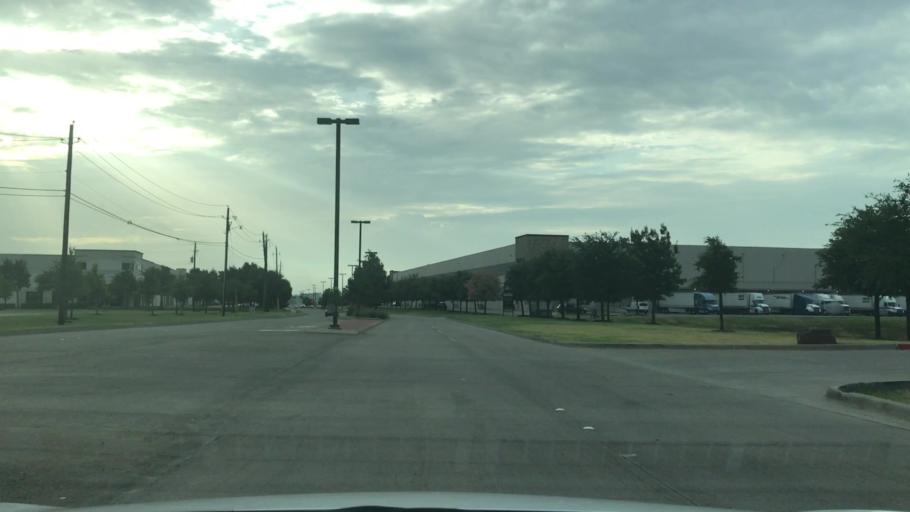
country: US
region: Texas
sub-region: Dallas County
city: Coppell
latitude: 32.9549
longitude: -97.0168
